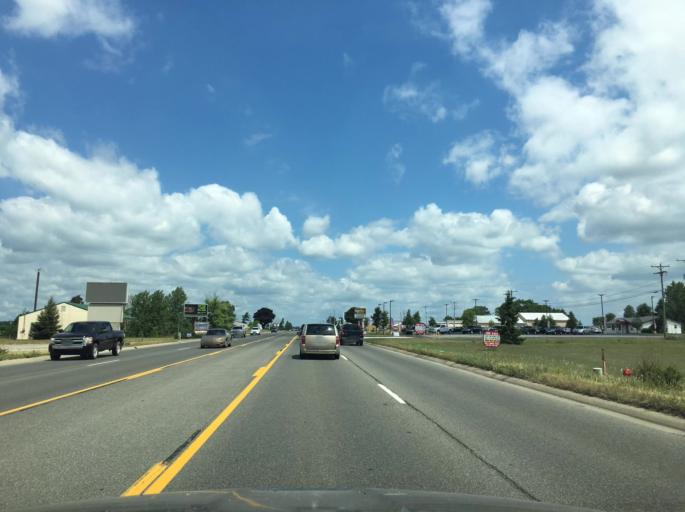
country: US
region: Michigan
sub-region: Grand Traverse County
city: Traverse City
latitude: 44.6789
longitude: -85.6563
